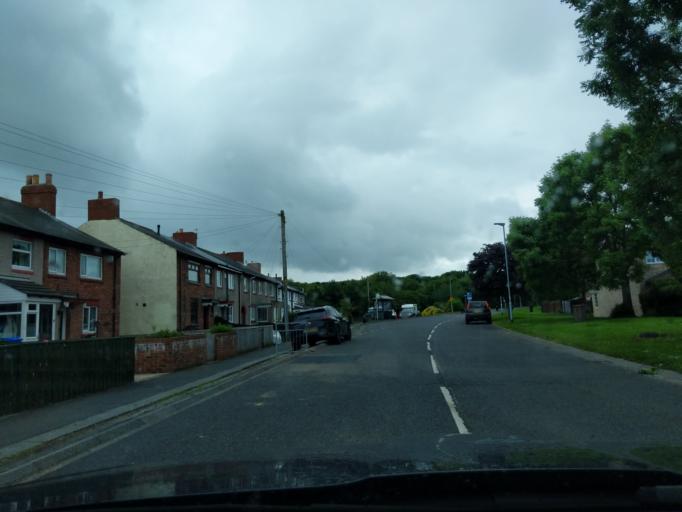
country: GB
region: England
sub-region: Northumberland
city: Seaton Delaval
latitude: 55.0820
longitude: -1.5247
